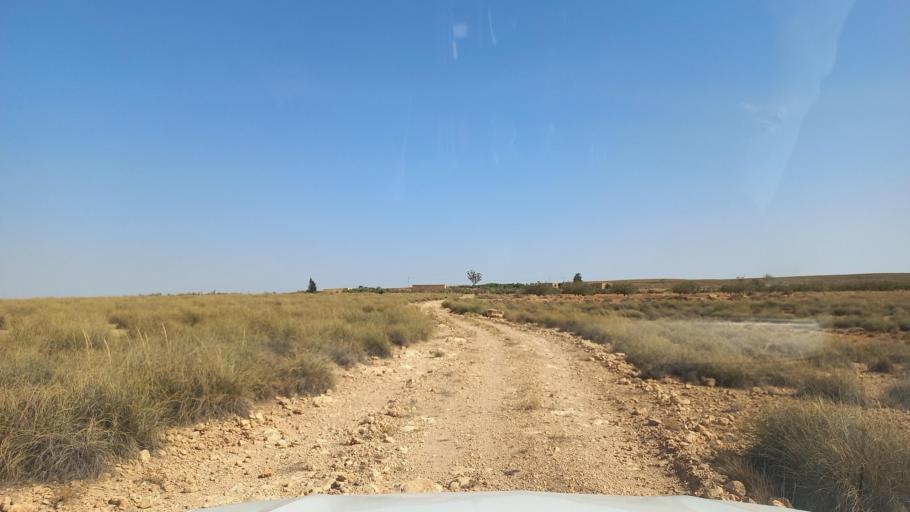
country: TN
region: Al Qasrayn
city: Kasserine
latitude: 35.2139
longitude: 8.9842
